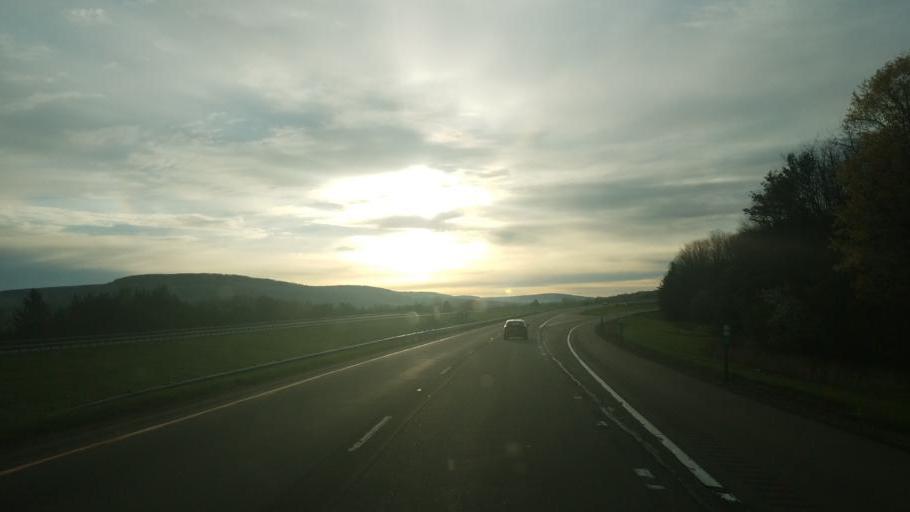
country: US
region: New York
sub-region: Allegany County
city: Belmont
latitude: 42.3007
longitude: -78.0198
